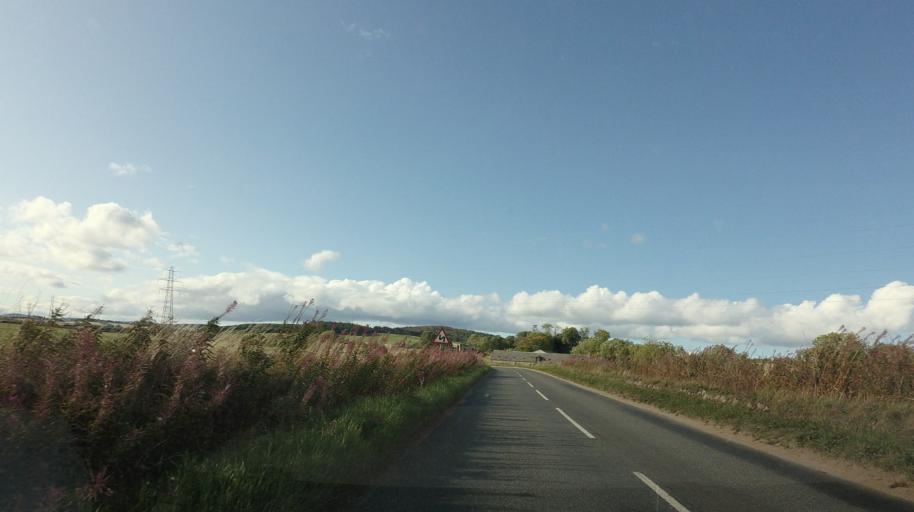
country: GB
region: Scotland
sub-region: Aberdeenshire
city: Banchory
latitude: 57.1342
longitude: -2.4285
